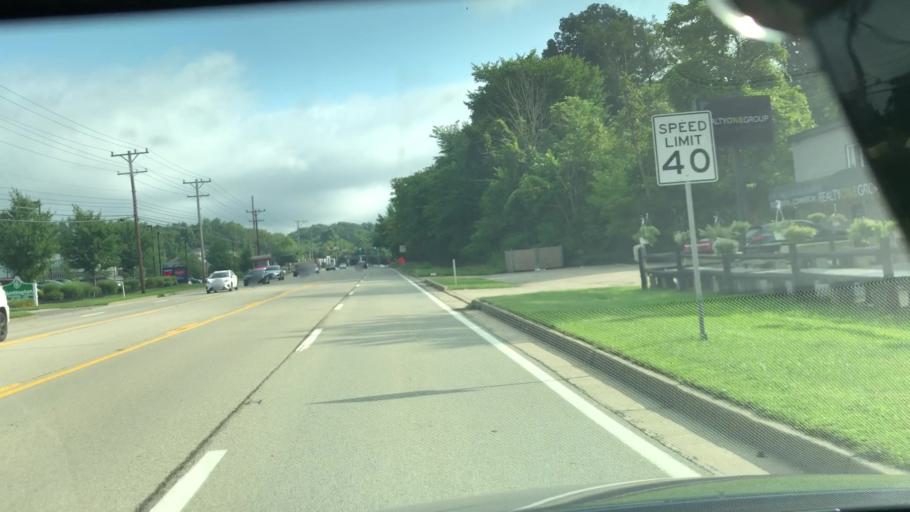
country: US
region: Pennsylvania
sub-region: Allegheny County
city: Bryn Mawr
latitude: 40.3019
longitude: -80.0977
